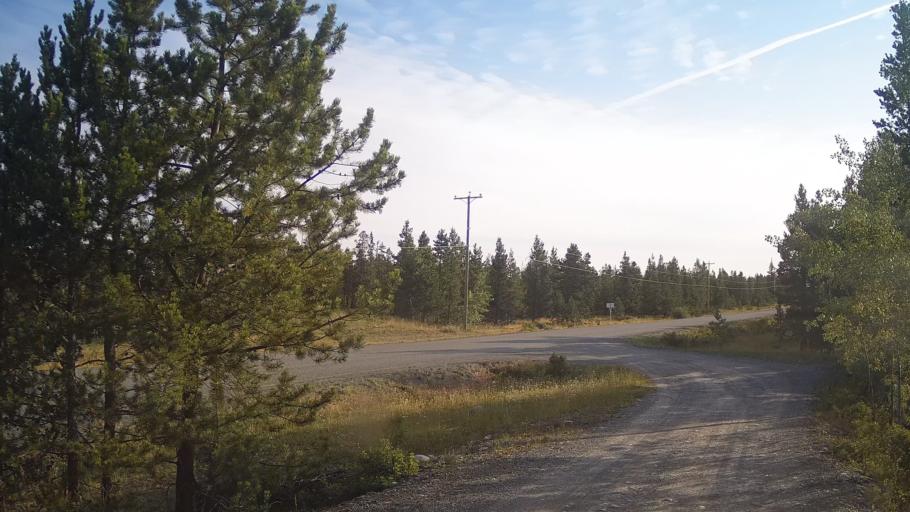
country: CA
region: British Columbia
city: Hanceville
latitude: 51.9532
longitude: -124.4417
